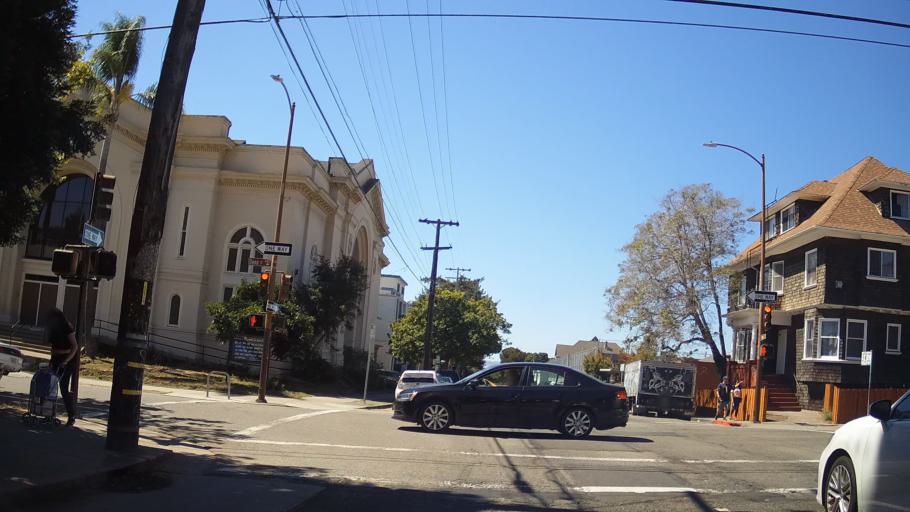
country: US
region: California
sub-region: Alameda County
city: Berkeley
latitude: 37.8658
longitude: -122.2610
